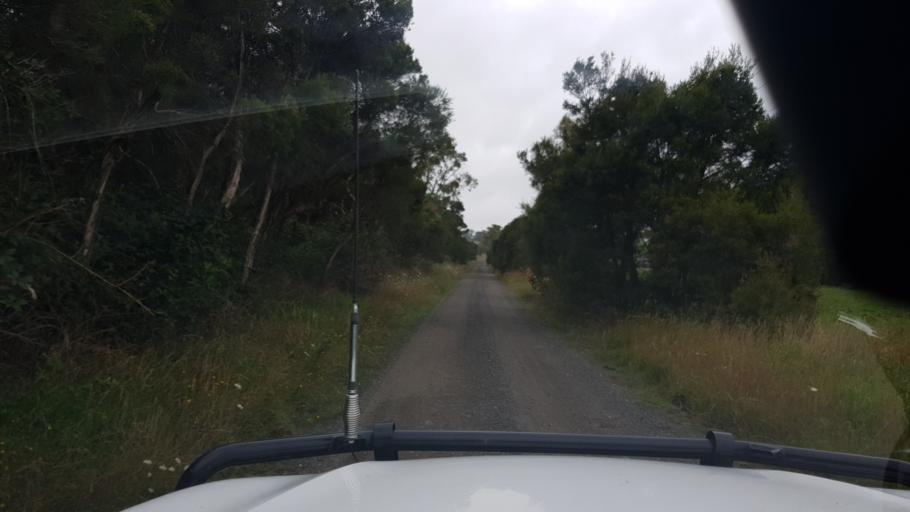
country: AU
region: Victoria
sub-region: Cardinia
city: Bunyip
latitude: -38.1170
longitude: 145.7790
